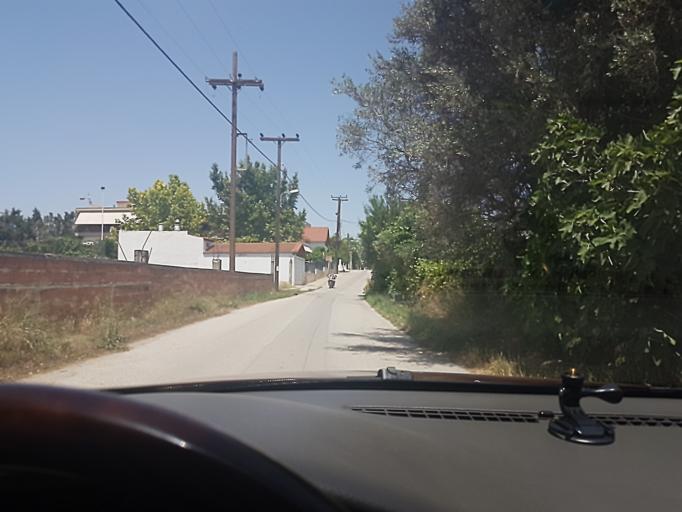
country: GR
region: Central Greece
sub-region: Nomos Evvoias
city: Vasilikon
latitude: 38.4218
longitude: 23.6679
